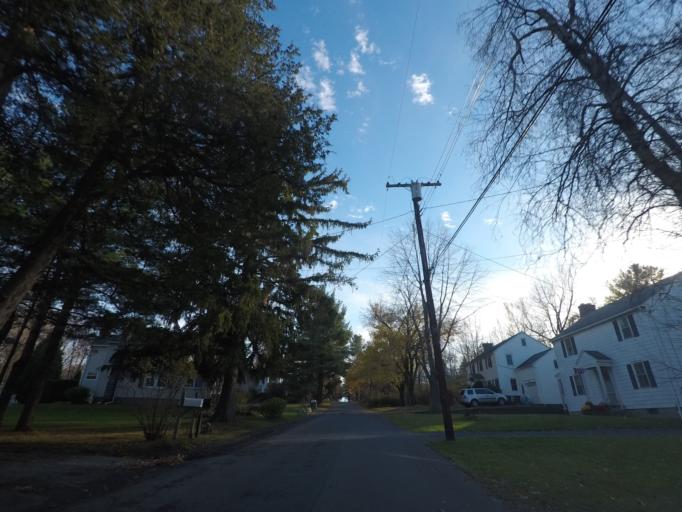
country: US
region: New York
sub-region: Rensselaer County
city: Averill Park
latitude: 42.6325
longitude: -73.5529
